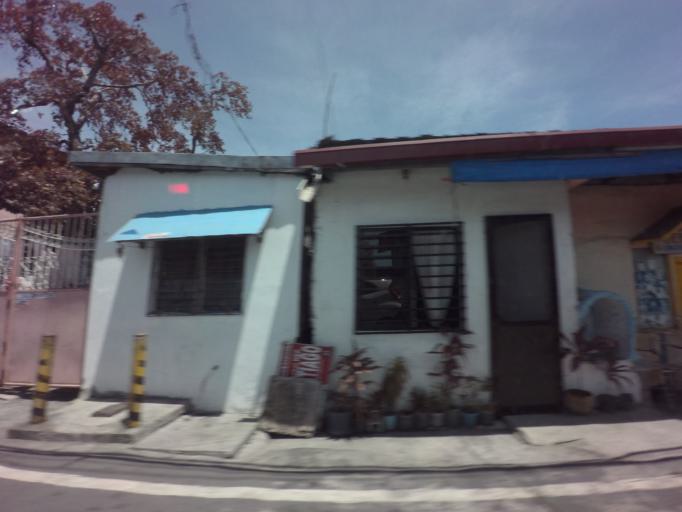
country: PH
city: Sambayanihan People's Village
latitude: 14.4601
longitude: 121.0540
